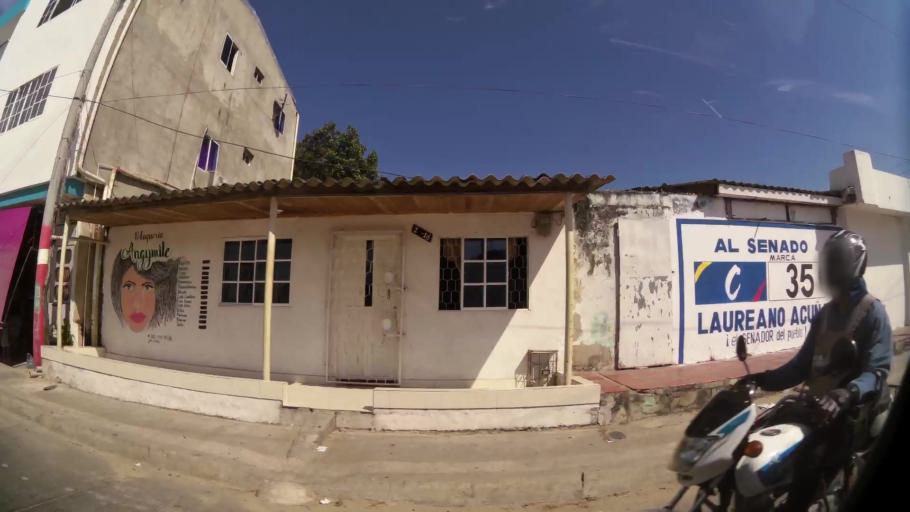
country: CO
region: Atlantico
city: Barranquilla
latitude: 10.9370
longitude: -74.8249
